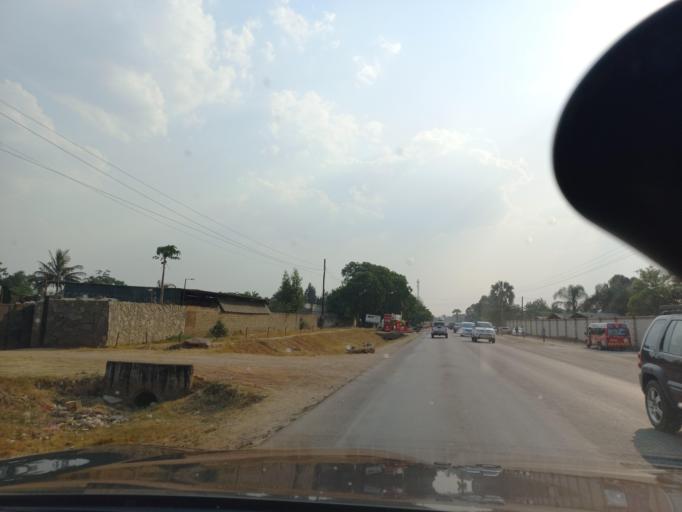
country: ZM
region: Lusaka
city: Lusaka
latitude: -15.4596
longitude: 28.2543
